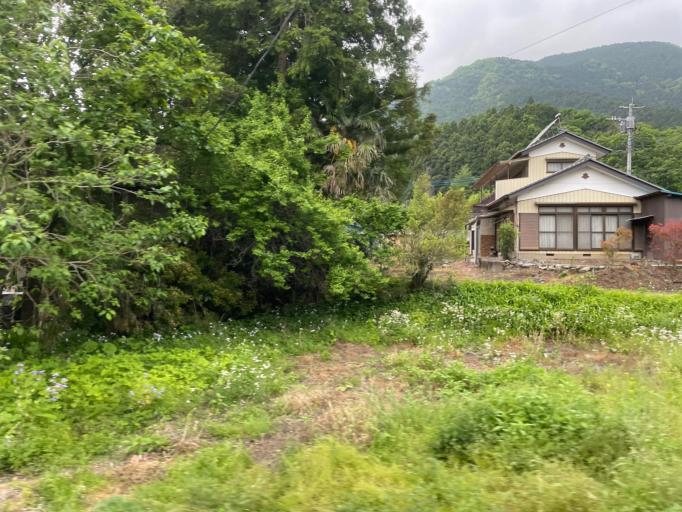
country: JP
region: Tochigi
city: Tanuma
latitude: 36.4589
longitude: 139.6365
